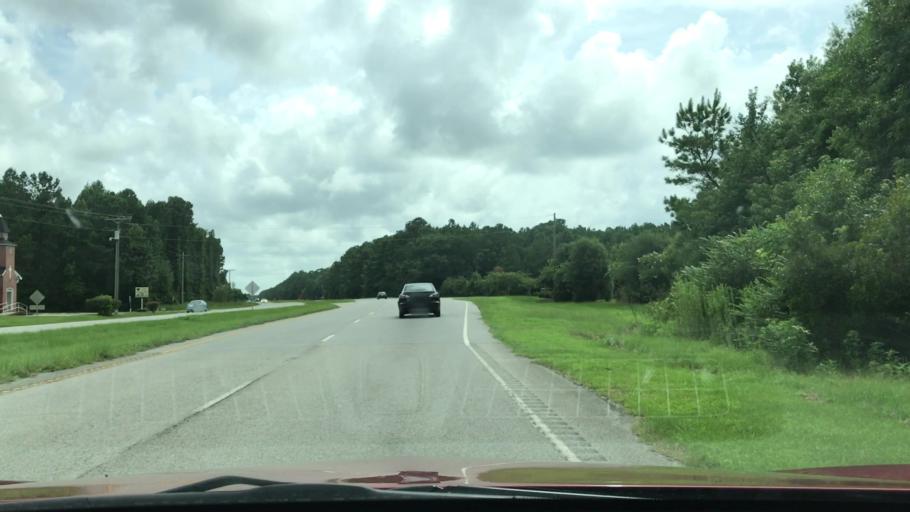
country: US
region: South Carolina
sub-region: Charleston County
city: Awendaw
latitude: 33.0286
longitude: -79.6272
